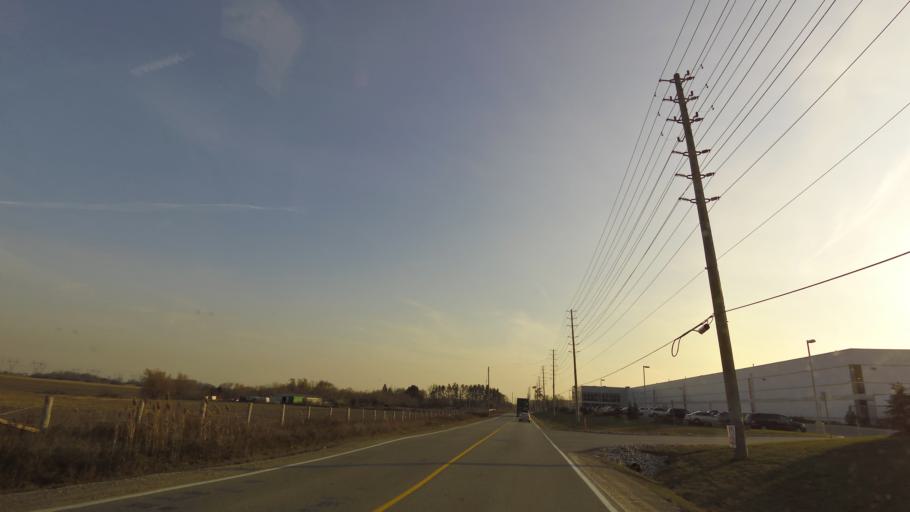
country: CA
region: Ontario
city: Vaughan
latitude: 43.8008
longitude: -79.6546
